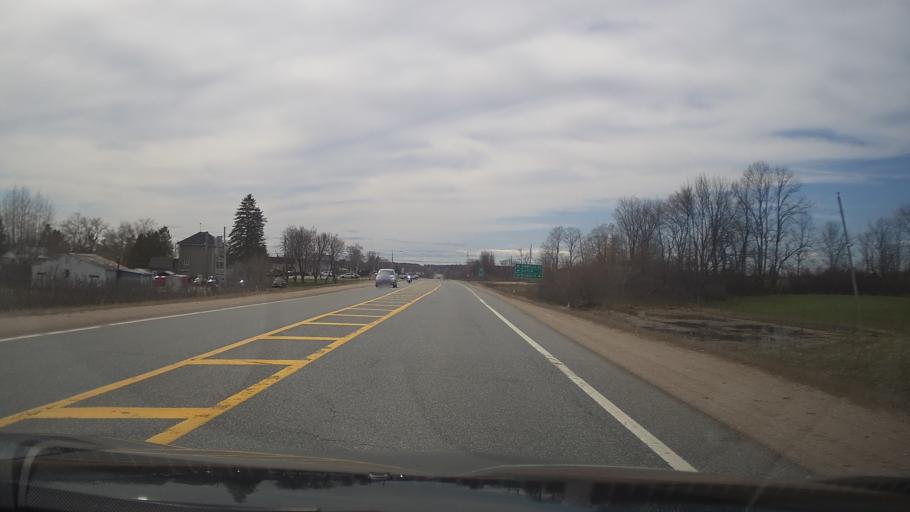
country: CA
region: Ontario
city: Arnprior
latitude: 45.5274
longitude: -76.2360
